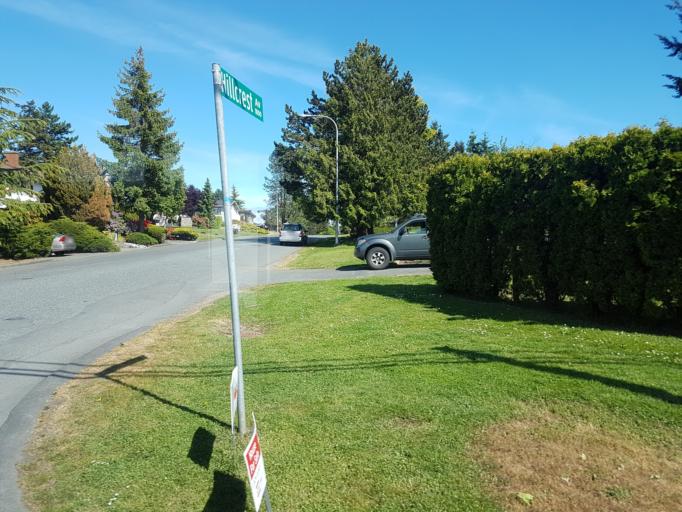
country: CA
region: British Columbia
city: Oak Bay
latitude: 48.4849
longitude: -123.3204
